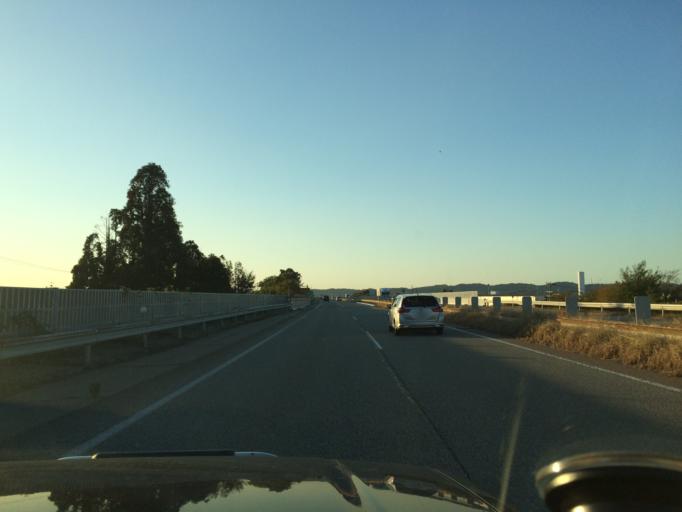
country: JP
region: Toyama
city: Toyama-shi
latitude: 36.6595
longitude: 137.1988
